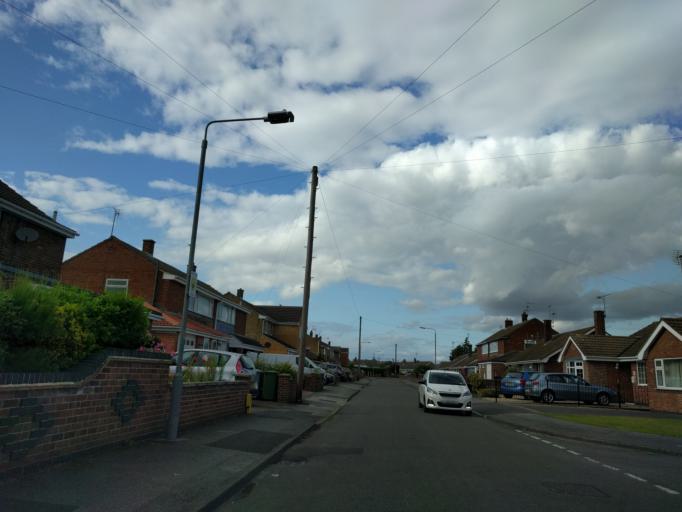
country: GB
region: England
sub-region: Nottinghamshire
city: Newark on Trent
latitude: 53.0619
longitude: -0.7795
